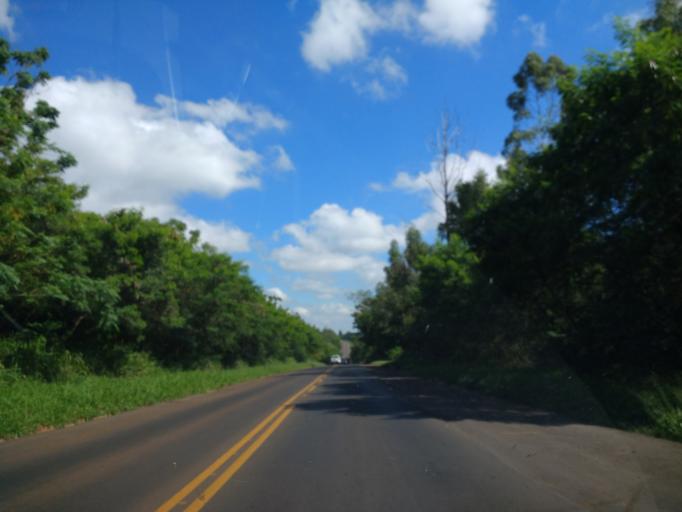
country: BR
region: Parana
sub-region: Umuarama
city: Umuarama
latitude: -23.8171
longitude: -53.3319
